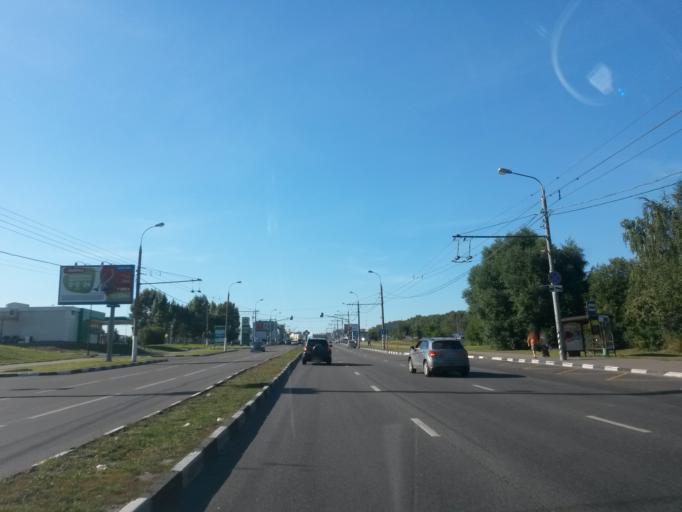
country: RU
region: Moscow
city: Yasenevo
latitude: 55.6101
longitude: 37.5201
